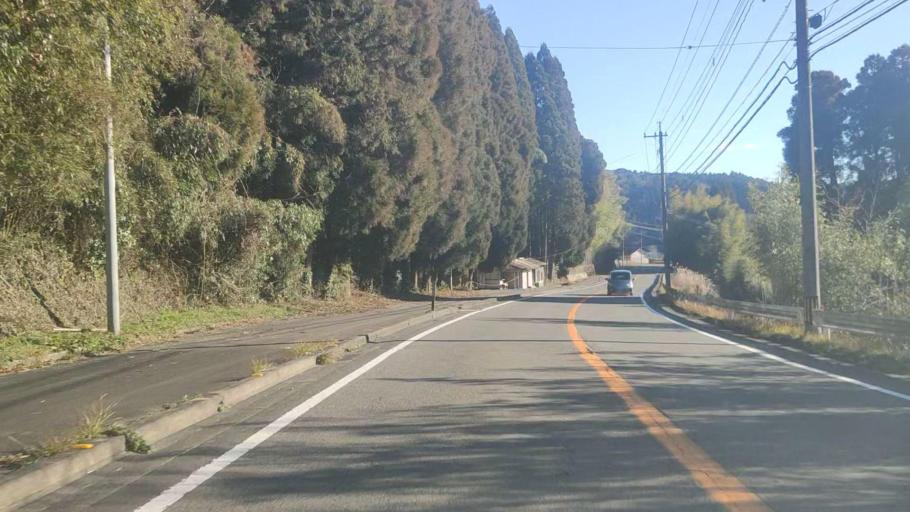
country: JP
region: Fukuoka
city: Maebaru-chuo
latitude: 33.4558
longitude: 130.2751
